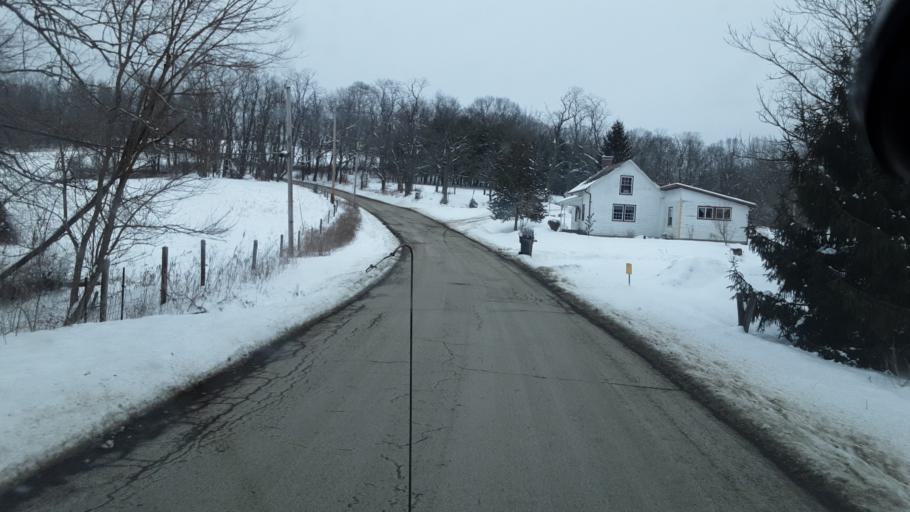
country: US
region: Ohio
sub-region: Muskingum County
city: Zanesville
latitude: 39.9432
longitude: -82.1709
